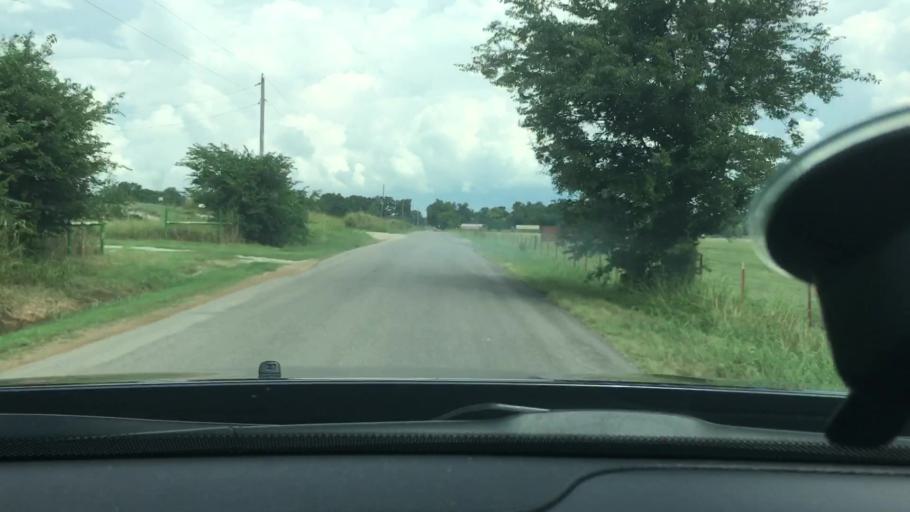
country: US
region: Oklahoma
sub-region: Carter County
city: Dickson
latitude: 34.1975
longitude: -96.8982
